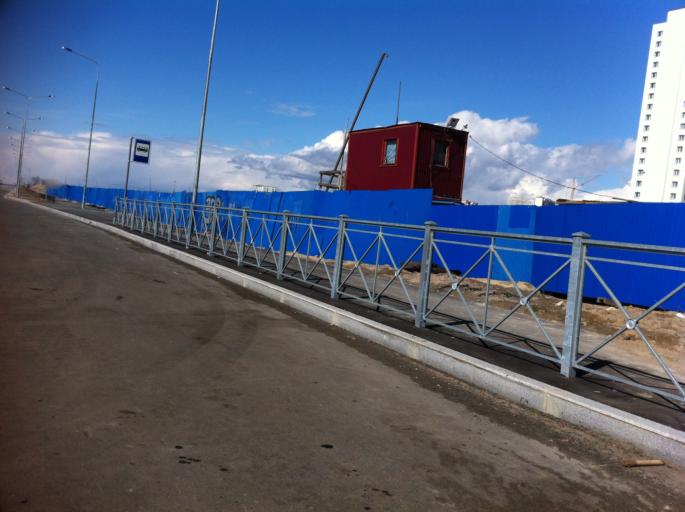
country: RU
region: St.-Petersburg
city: Sosnovaya Polyana
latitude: 59.8599
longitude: 30.1571
